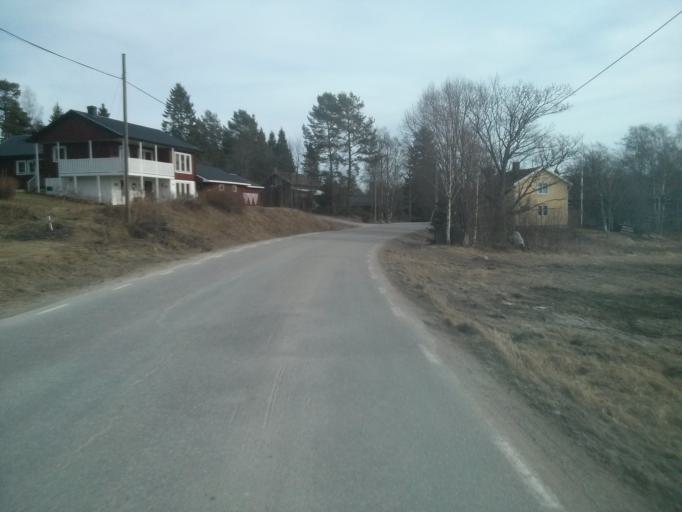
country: SE
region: Vaesternorrland
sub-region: Sundsvalls Kommun
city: Njurundabommen
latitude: 62.2353
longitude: 17.3995
